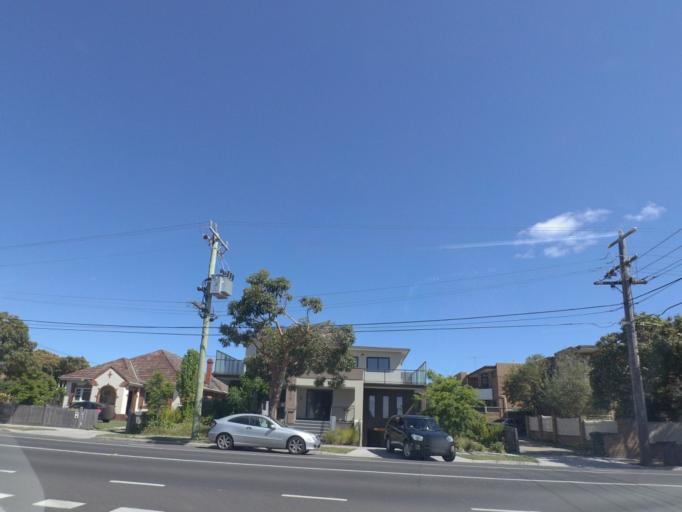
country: AU
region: Victoria
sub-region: Monash
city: Chadstone
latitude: -37.8996
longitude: 145.0964
